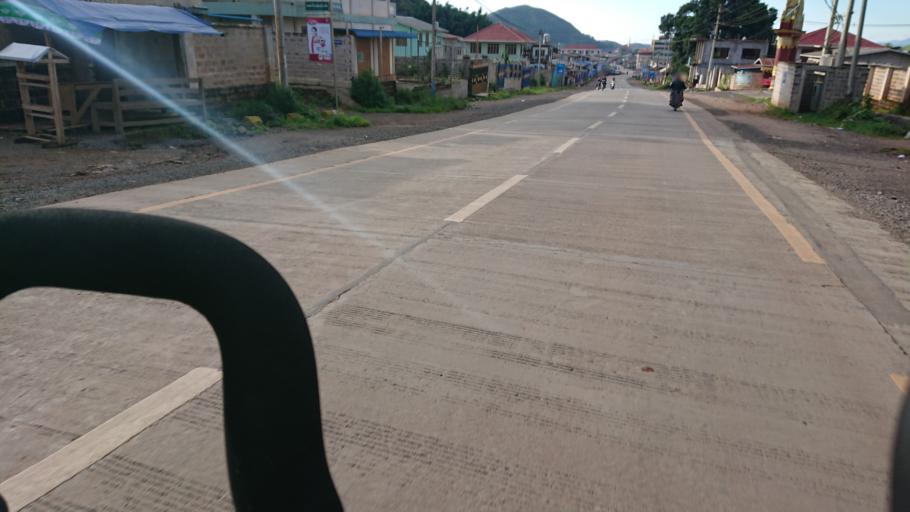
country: MM
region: Shan
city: Taunggyi
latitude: 20.7409
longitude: 97.0512
